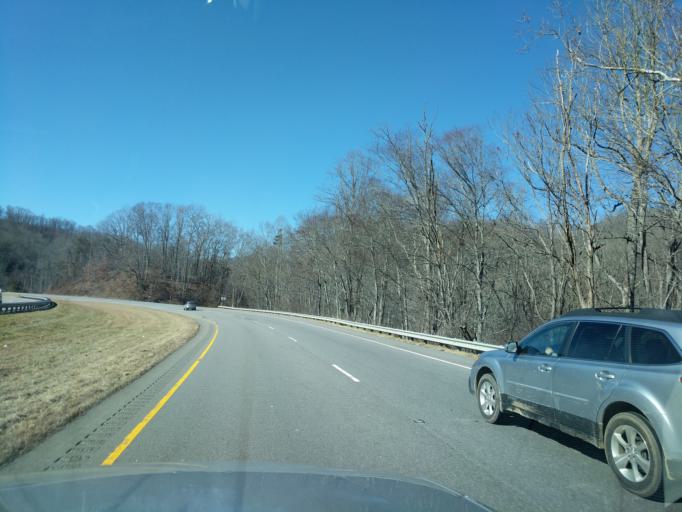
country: US
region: North Carolina
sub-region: Jackson County
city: Cullowhee
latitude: 35.3976
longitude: -83.1309
